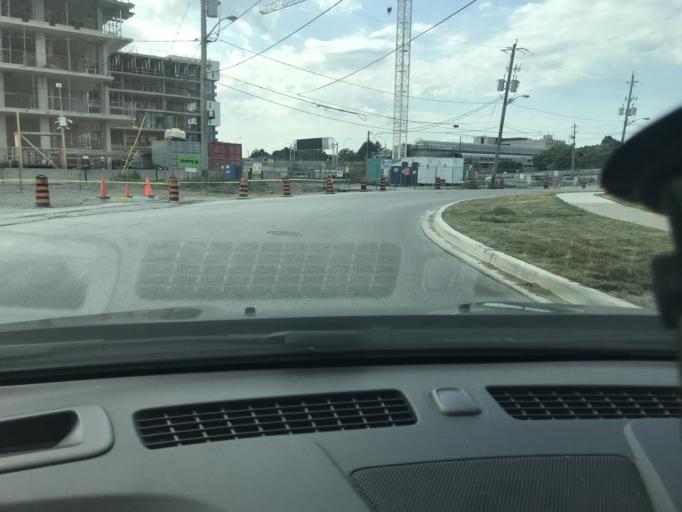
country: CA
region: Ontario
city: Toronto
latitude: 43.7229
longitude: -79.4450
